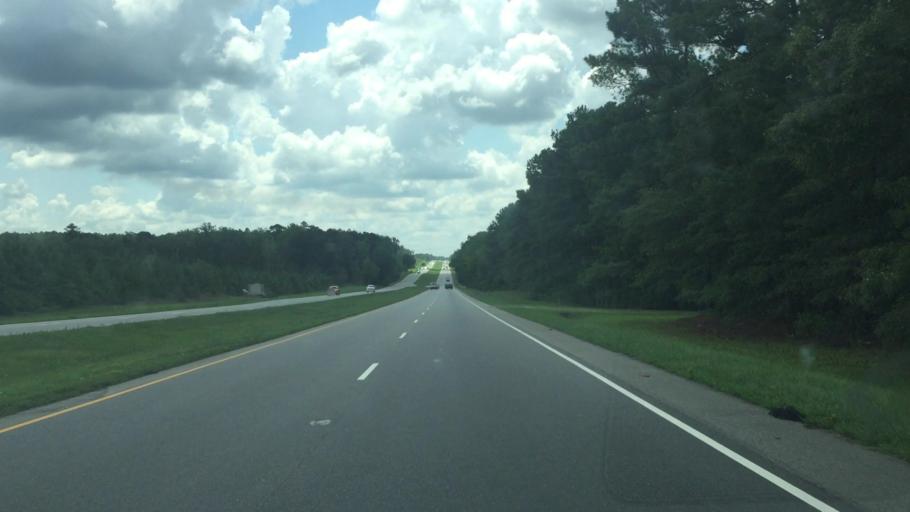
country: US
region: North Carolina
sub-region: Richmond County
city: Hamlet
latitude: 34.8596
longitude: -79.6308
